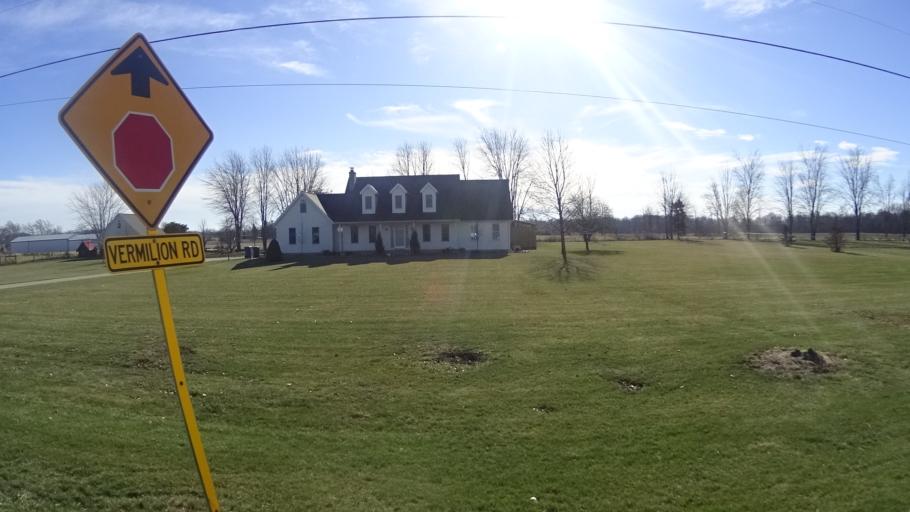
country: US
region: Ohio
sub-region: Lorain County
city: Camden
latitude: 41.2873
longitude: -82.3045
